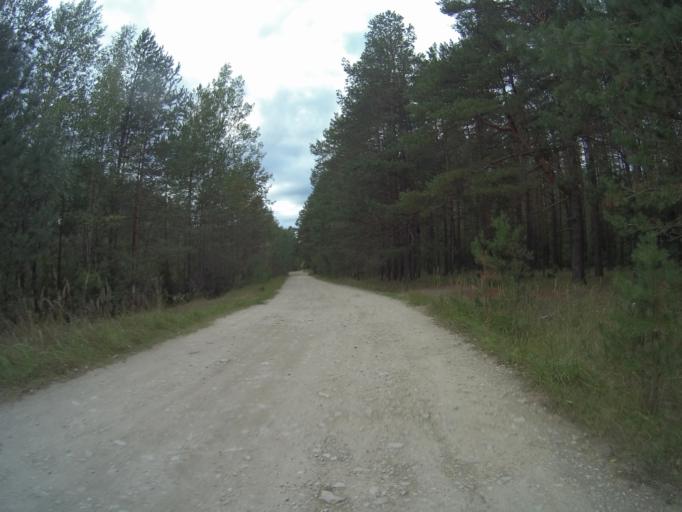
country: RU
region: Vladimir
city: Golovino
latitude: 55.9441
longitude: 40.4586
